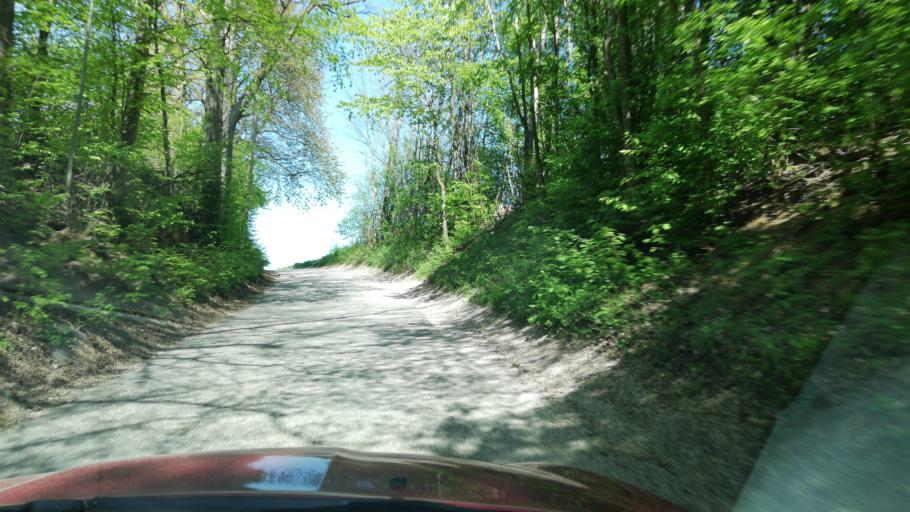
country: AT
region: Upper Austria
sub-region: Politischer Bezirk Kirchdorf an der Krems
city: Kremsmunster
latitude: 48.0481
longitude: 14.1558
